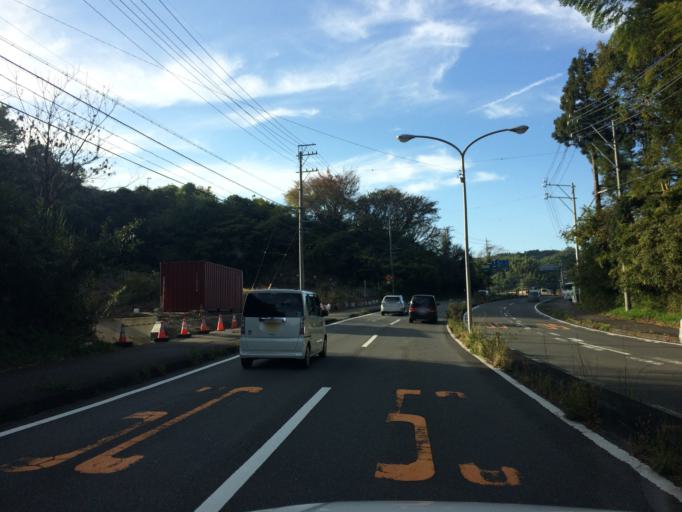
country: JP
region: Shizuoka
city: Fujieda
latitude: 34.8682
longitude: 138.2310
